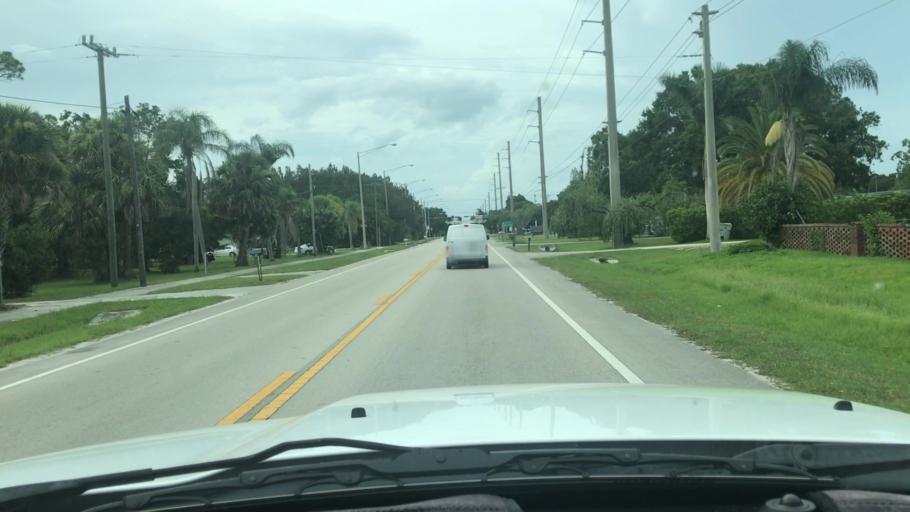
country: US
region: Florida
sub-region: Indian River County
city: Vero Beach South
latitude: 27.6138
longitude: -80.4139
